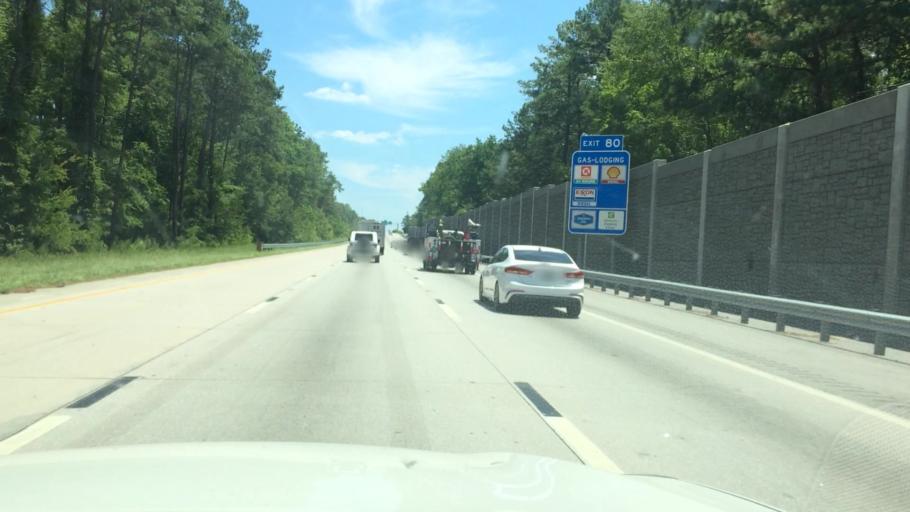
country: US
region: South Carolina
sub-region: Richland County
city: Woodfield
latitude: 34.0899
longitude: -80.8672
